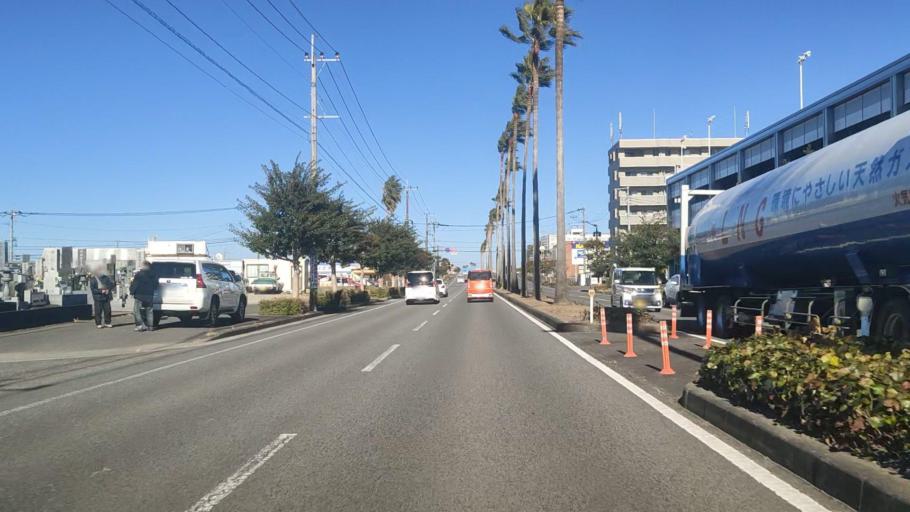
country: JP
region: Miyazaki
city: Miyazaki-shi
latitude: 31.9173
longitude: 131.4500
